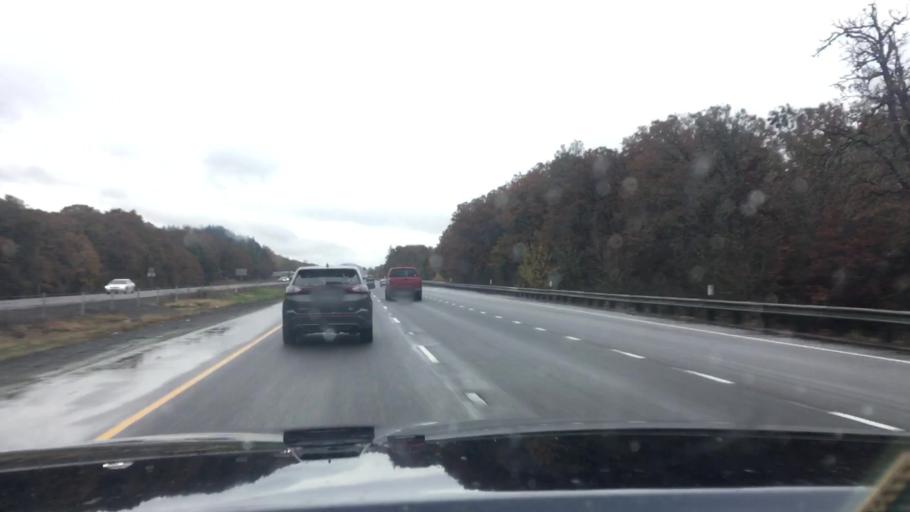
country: US
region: Oregon
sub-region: Lane County
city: Springfield
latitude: 43.9931
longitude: -123.0055
